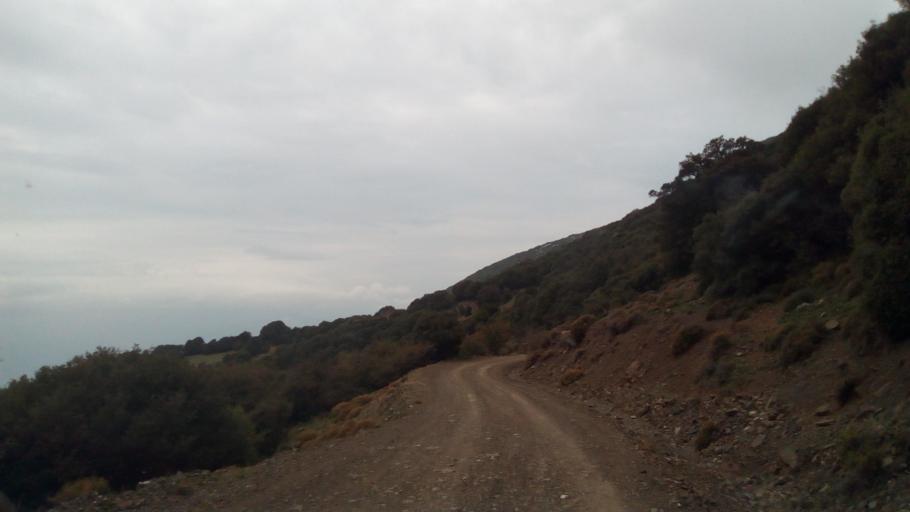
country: GR
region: West Greece
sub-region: Nomos Achaias
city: Selianitika
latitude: 38.4156
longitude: 22.0913
